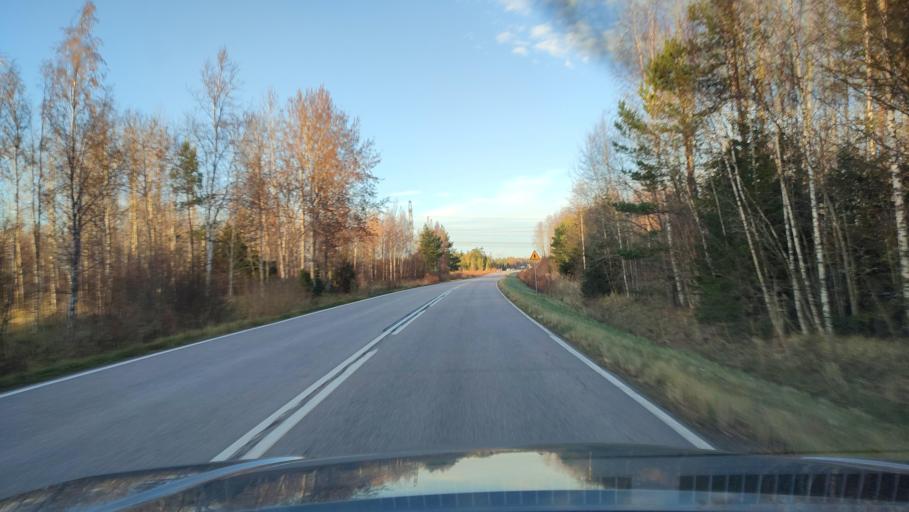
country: FI
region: Ostrobothnia
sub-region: Sydosterbotten
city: Kristinestad
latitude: 62.2894
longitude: 21.3779
